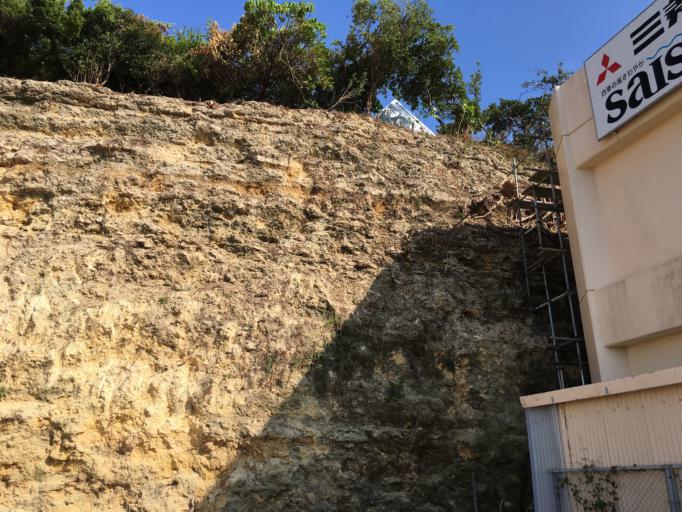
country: JP
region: Okinawa
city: Naha-shi
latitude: 26.2318
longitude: 127.6845
